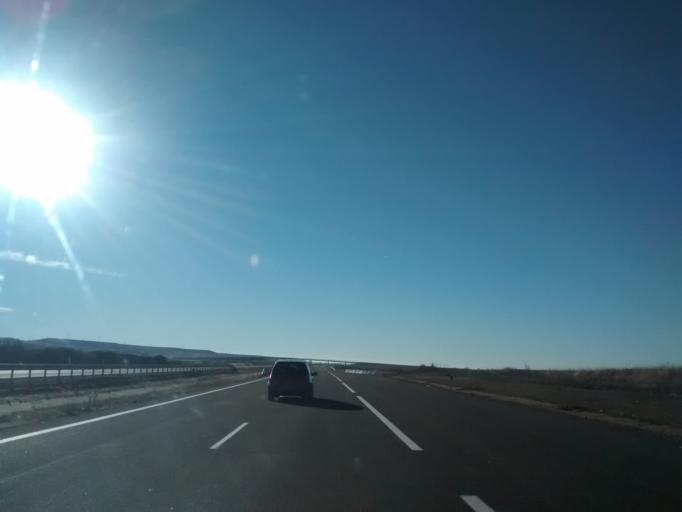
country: ES
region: Castille and Leon
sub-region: Provincia de Palencia
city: Santa Cruz de Boedo
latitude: 42.5206
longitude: -4.3833
